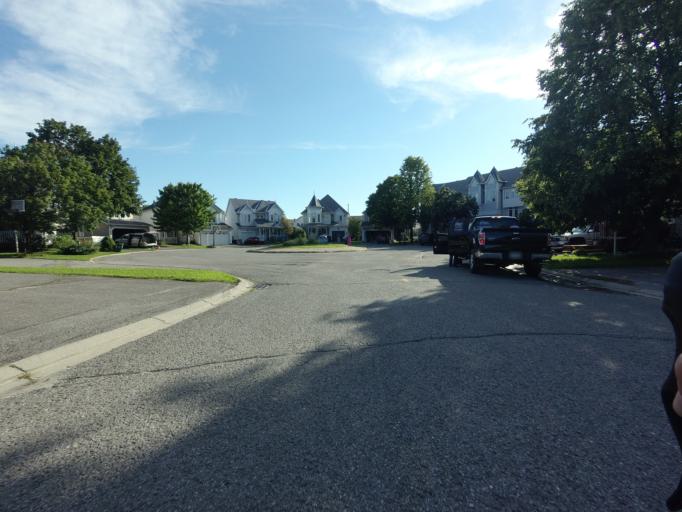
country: CA
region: Ontario
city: Bells Corners
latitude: 45.2958
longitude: -75.7360
